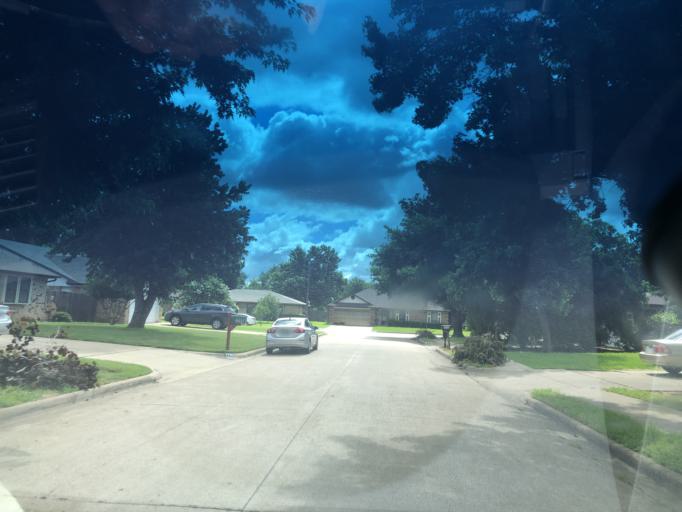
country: US
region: Texas
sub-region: Dallas County
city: Grand Prairie
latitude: 32.7071
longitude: -97.0358
